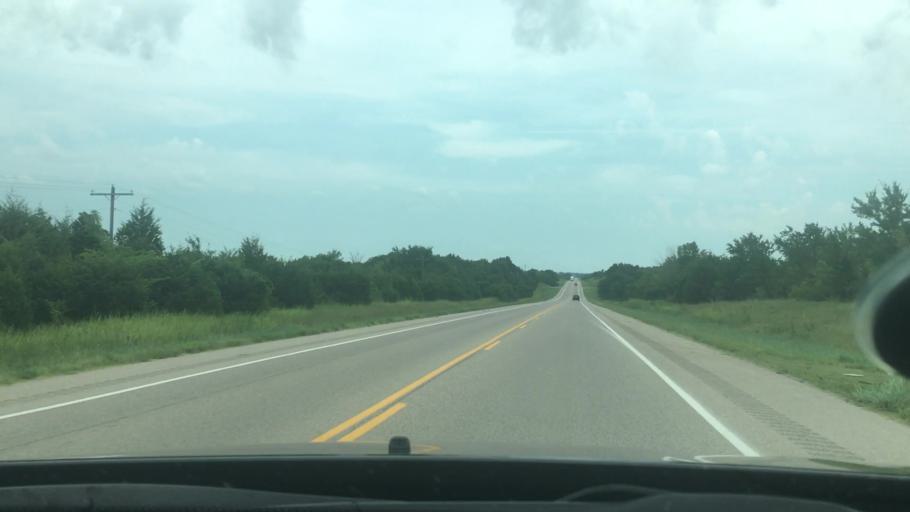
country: US
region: Oklahoma
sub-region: Seminole County
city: Konawa
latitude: 34.9875
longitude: -96.6793
